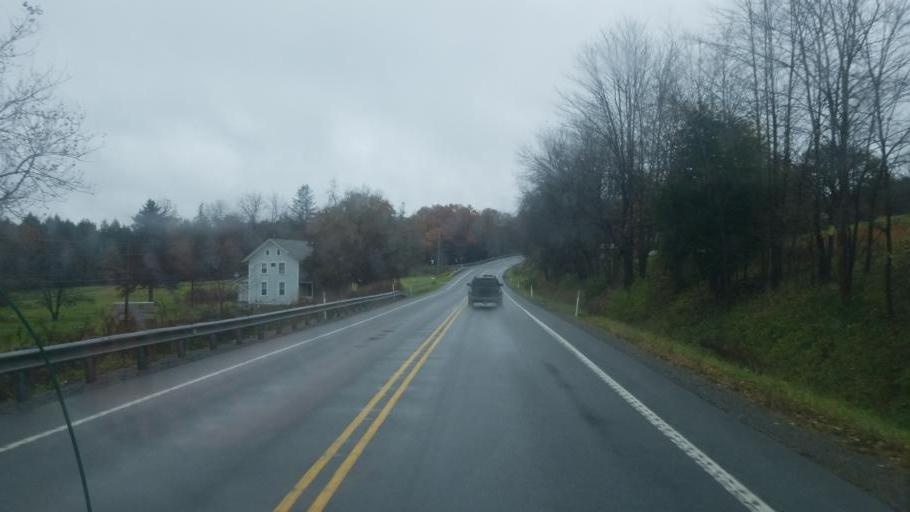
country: US
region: Pennsylvania
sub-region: Clearfield County
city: Shiloh
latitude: 41.1017
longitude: -78.2433
